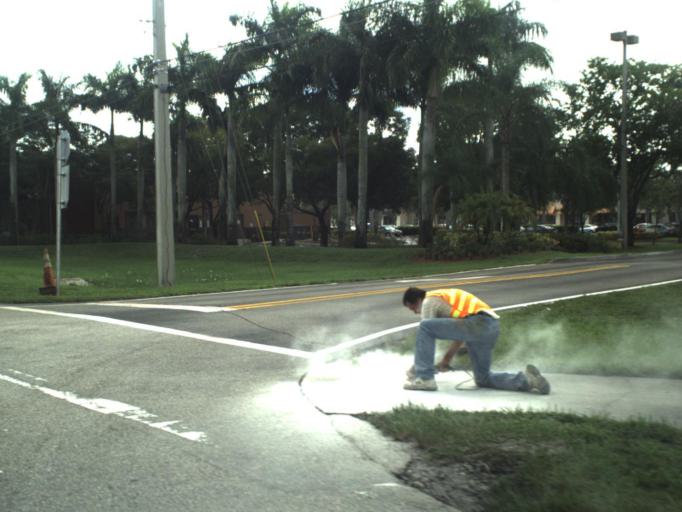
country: US
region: Florida
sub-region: Broward County
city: Sunshine Ranches
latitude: 26.0076
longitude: -80.3091
